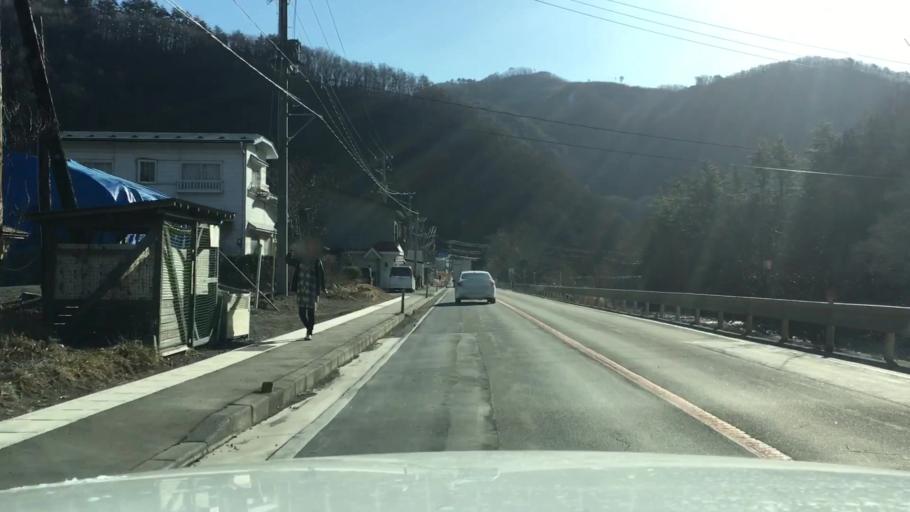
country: JP
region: Iwate
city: Miyako
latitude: 39.5939
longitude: 141.6622
